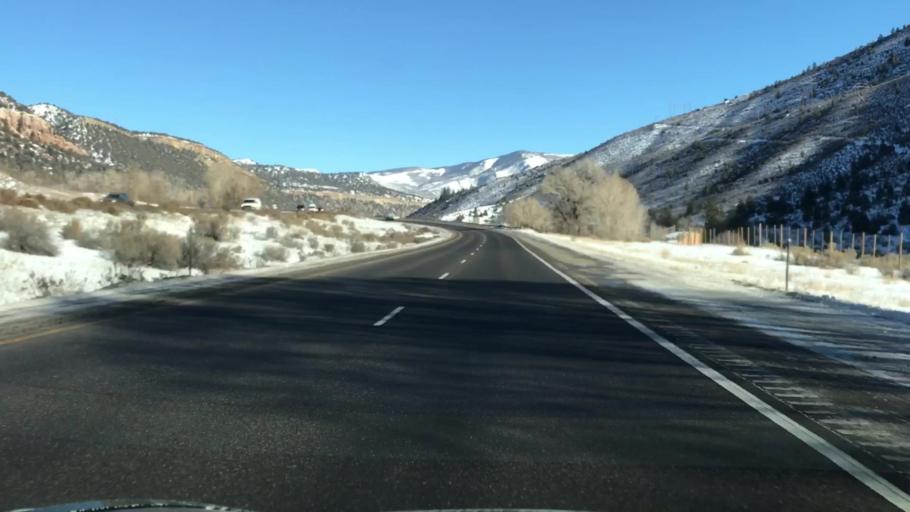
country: US
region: Colorado
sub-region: Eagle County
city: Eagle
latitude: 39.7060
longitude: -106.7242
